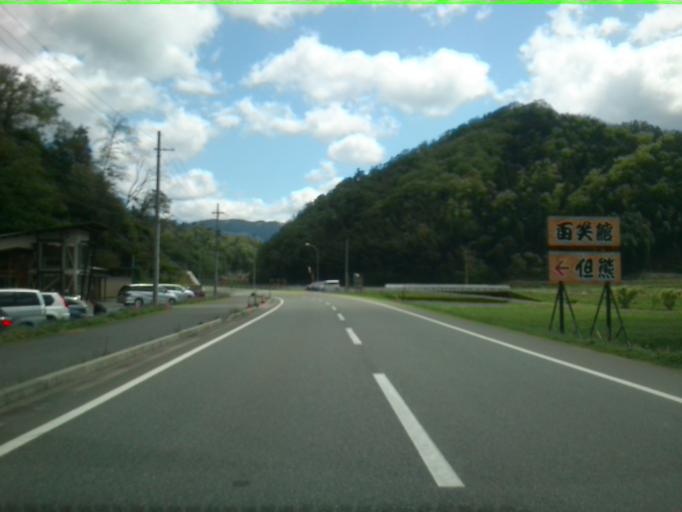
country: JP
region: Kyoto
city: Fukuchiyama
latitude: 35.4398
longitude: 134.9977
